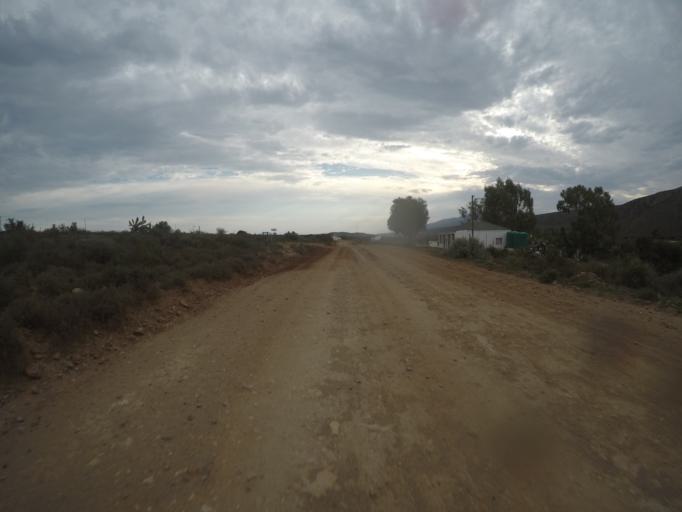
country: ZA
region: Eastern Cape
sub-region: Cacadu District Municipality
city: Willowmore
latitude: -33.4916
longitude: 23.5936
